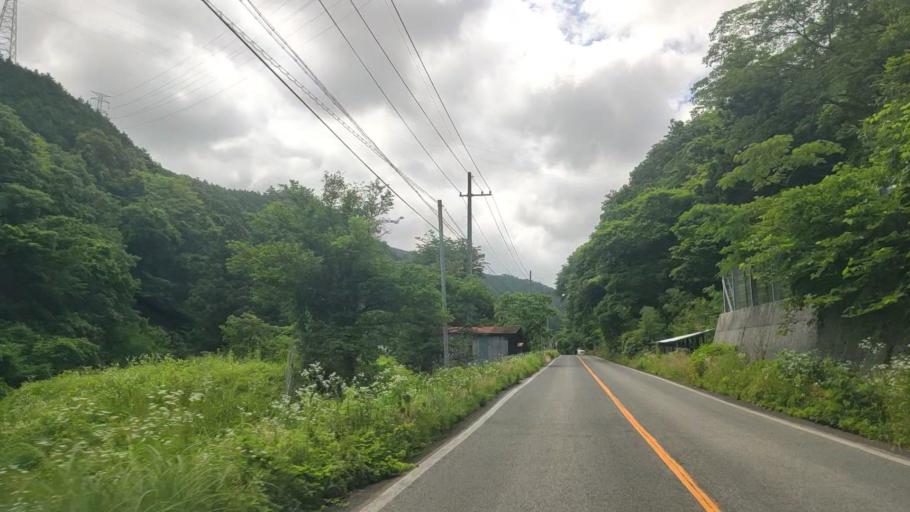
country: JP
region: Tottori
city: Yonago
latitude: 35.2819
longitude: 133.4283
